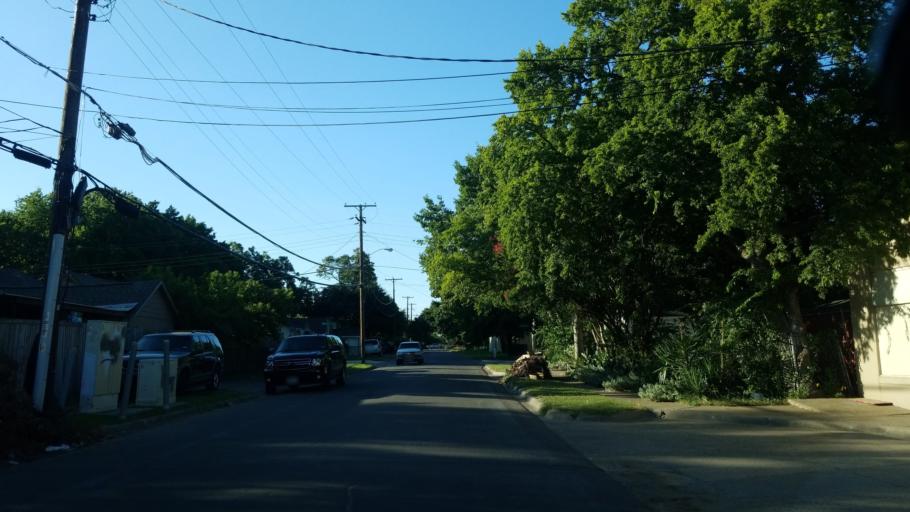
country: US
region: Texas
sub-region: Dallas County
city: Balch Springs
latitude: 32.7732
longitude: -96.6965
